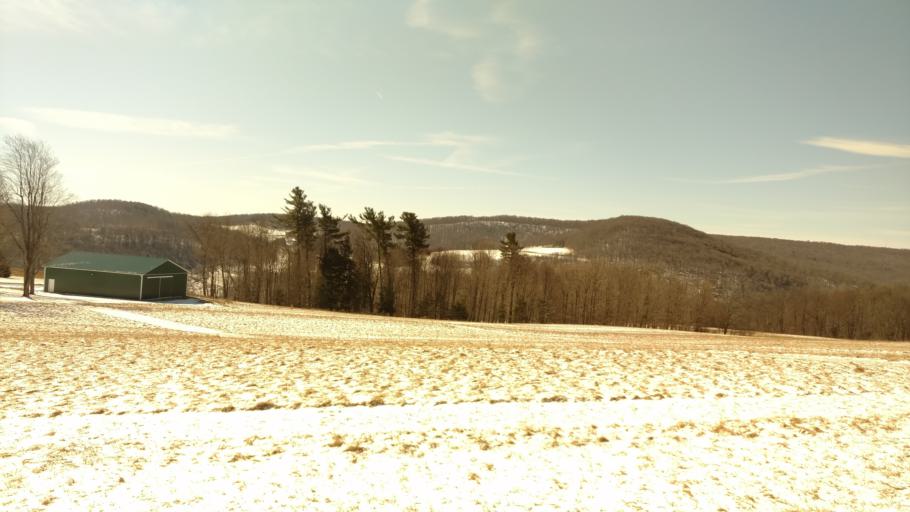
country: US
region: New York
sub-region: Allegany County
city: Wellsville
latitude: 42.0818
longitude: -77.9676
